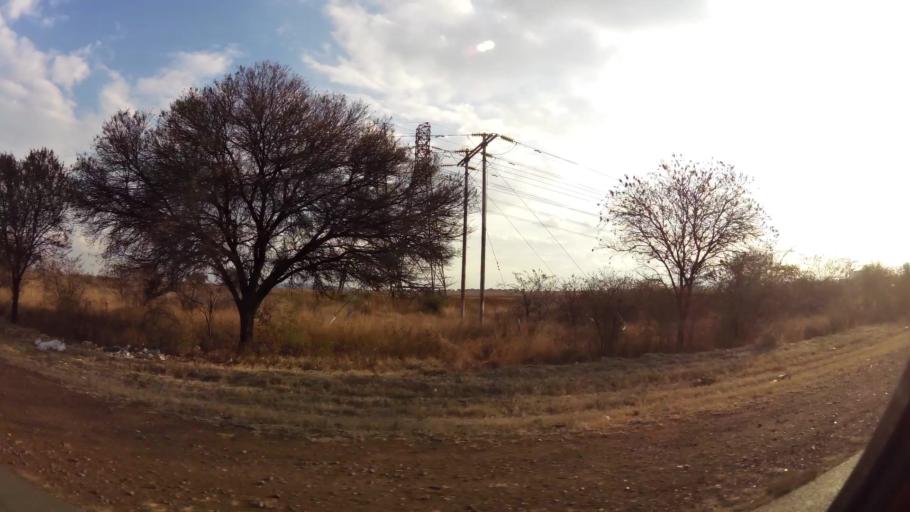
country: ZA
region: Gauteng
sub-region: Sedibeng District Municipality
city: Vereeniging
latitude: -26.6273
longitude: 27.8660
